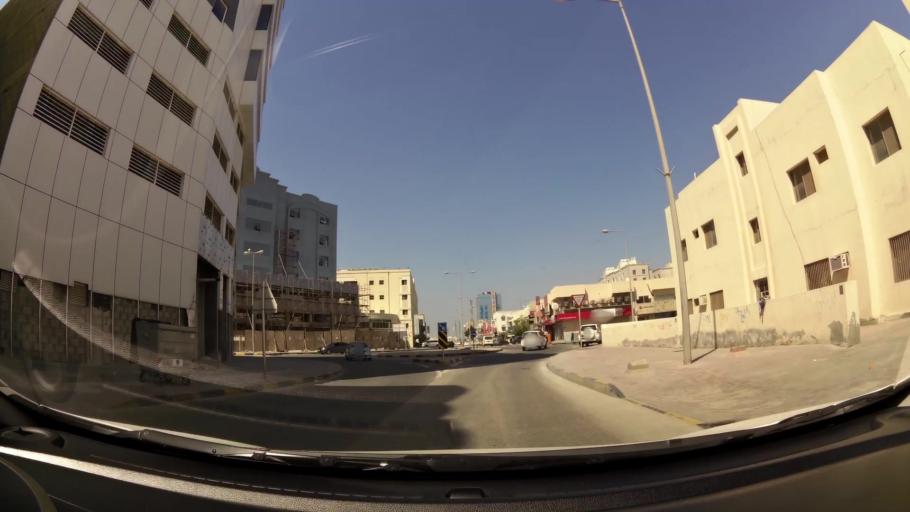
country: BH
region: Manama
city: Manama
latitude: 26.2034
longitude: 50.5968
